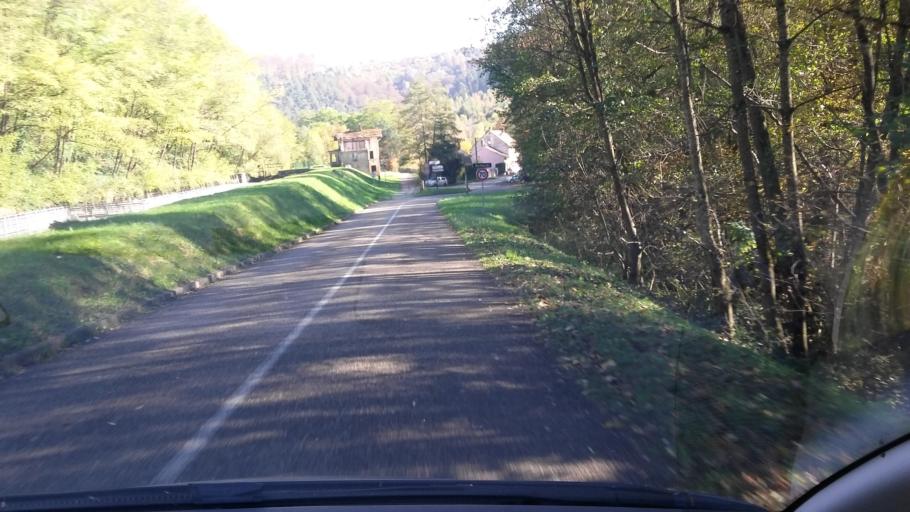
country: FR
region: Lorraine
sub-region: Departement de la Moselle
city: Phalsbourg
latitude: 48.7198
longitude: 7.2195
